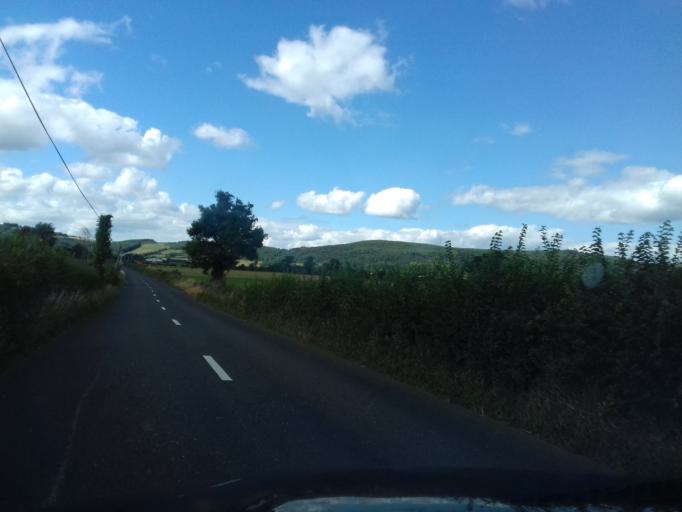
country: IE
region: Munster
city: Carrick-on-Suir
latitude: 52.3760
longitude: -7.4522
